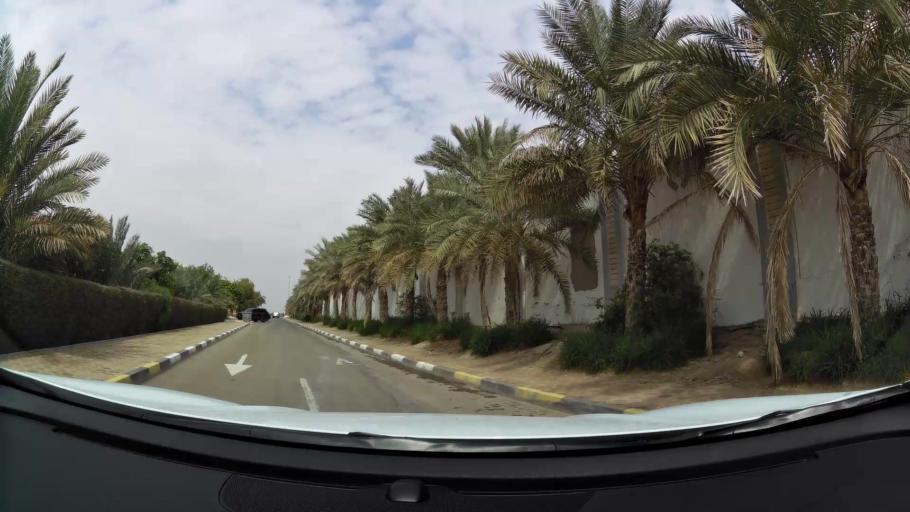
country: AE
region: Abu Dhabi
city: Al Ain
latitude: 24.2113
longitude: 55.7931
